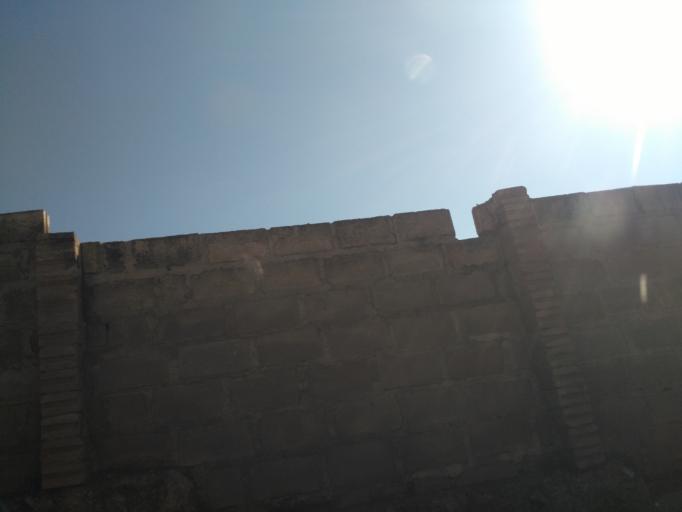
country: TZ
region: Mwanza
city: Mwanza
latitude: -2.5004
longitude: 32.8947
